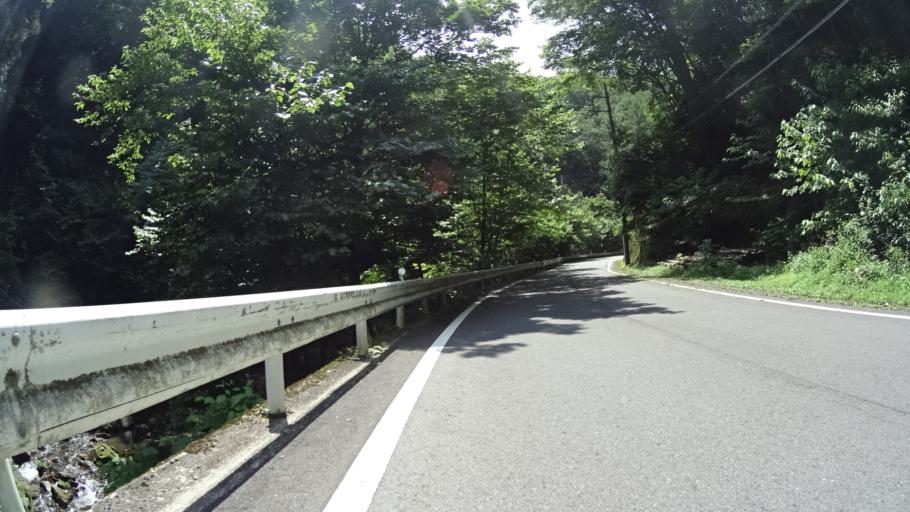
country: JP
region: Nagano
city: Saku
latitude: 36.0687
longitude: 138.7007
